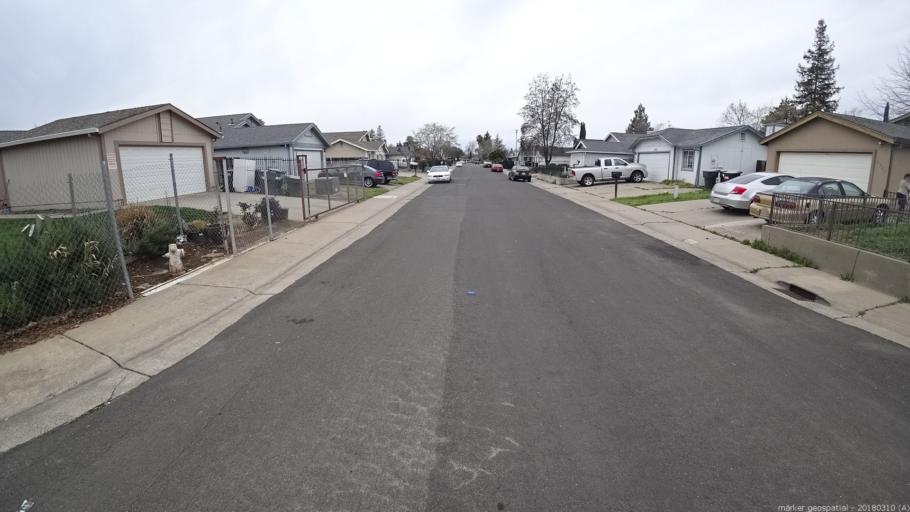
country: US
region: California
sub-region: Sacramento County
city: Florin
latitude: 38.4829
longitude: -121.4037
